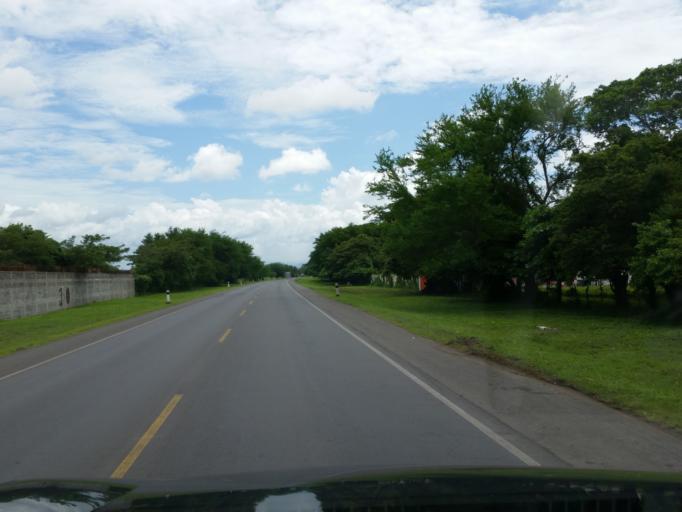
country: NI
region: Managua
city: Tipitapa
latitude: 12.1873
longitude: -86.1070
